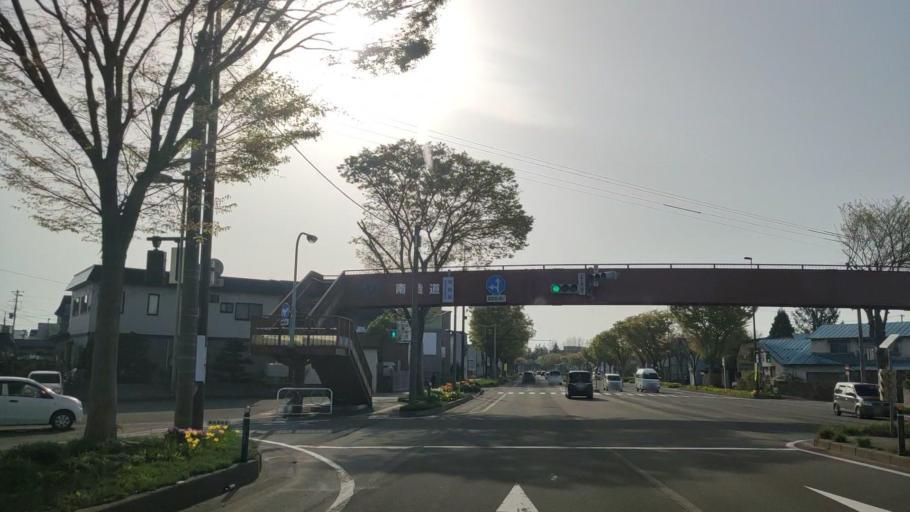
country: JP
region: Aomori
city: Aomori Shi
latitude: 40.8276
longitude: 140.7920
